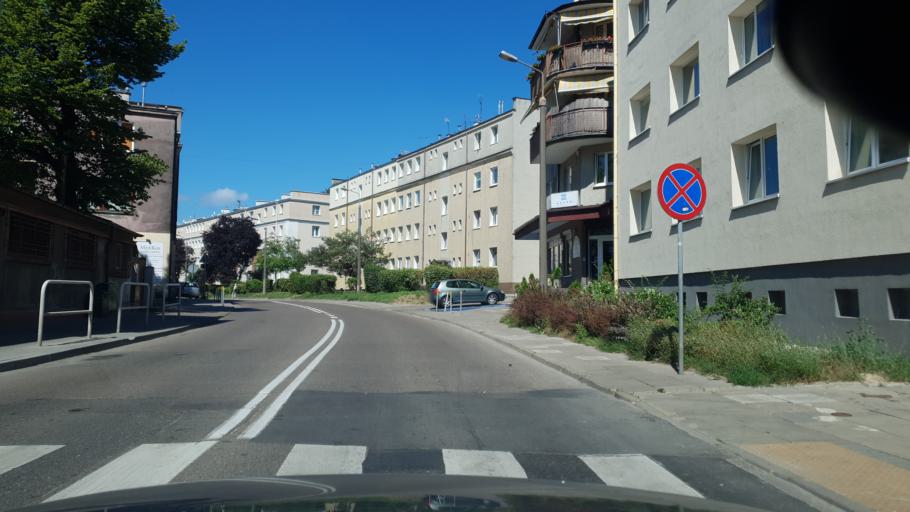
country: PL
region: Pomeranian Voivodeship
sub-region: Gdynia
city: Gdynia
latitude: 54.5035
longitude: 18.5424
